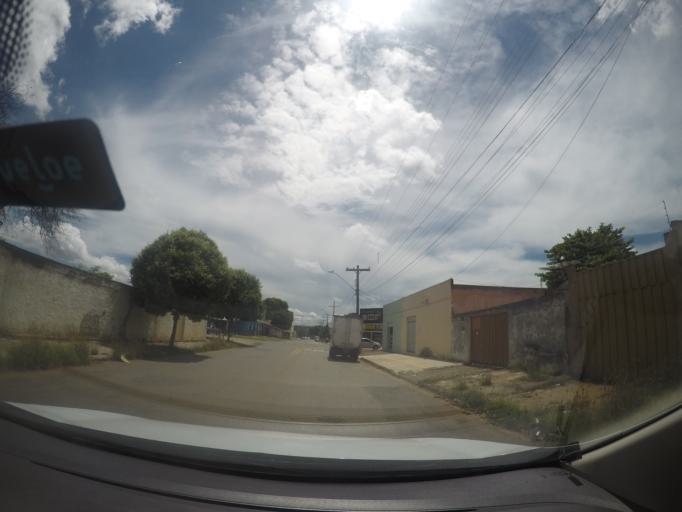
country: BR
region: Goias
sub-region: Goiania
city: Goiania
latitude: -16.6812
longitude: -49.3177
